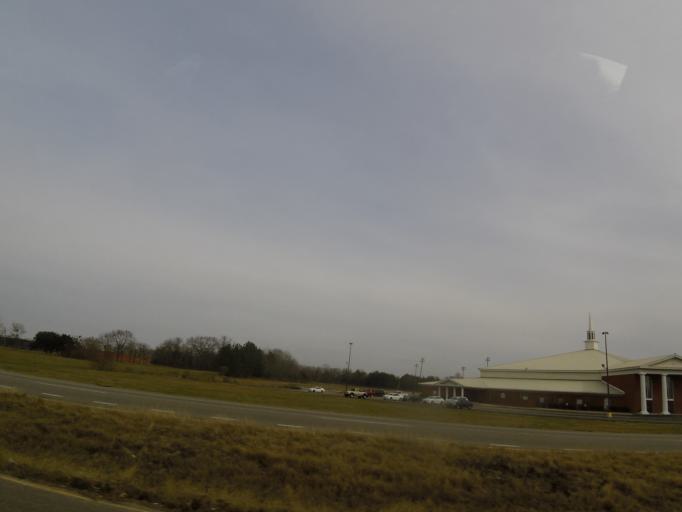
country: US
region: Alabama
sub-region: Montgomery County
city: Montgomery
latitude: 32.3095
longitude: -86.2194
